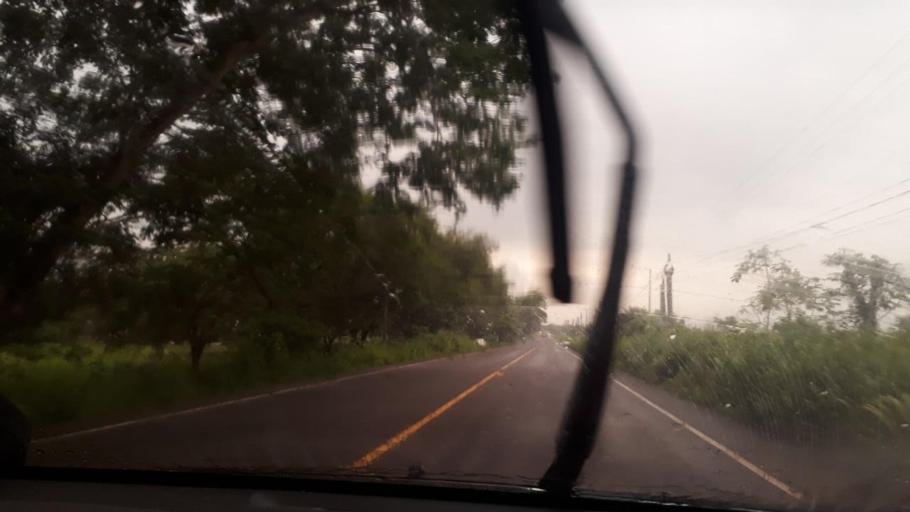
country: GT
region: Escuintla
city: Guanagazapa
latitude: 14.0985
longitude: -90.6064
